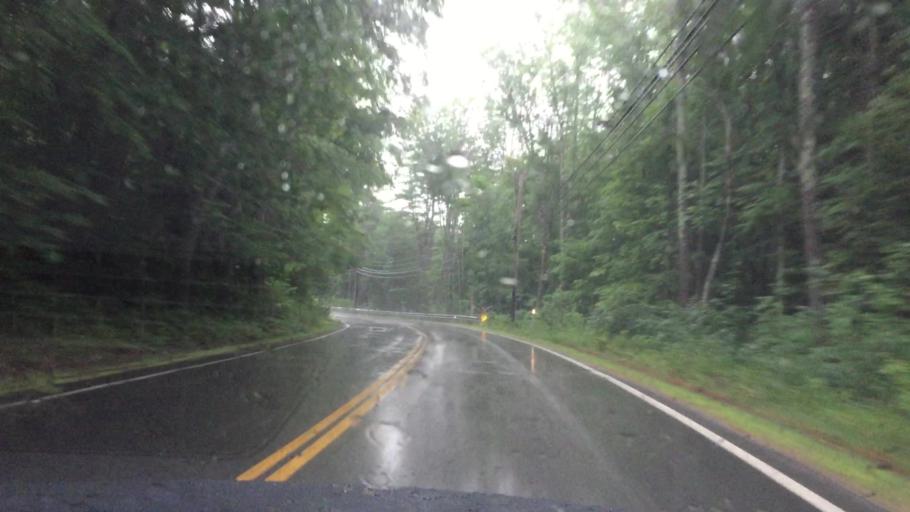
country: US
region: New Hampshire
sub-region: Belknap County
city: Meredith
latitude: 43.6932
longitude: -71.5148
